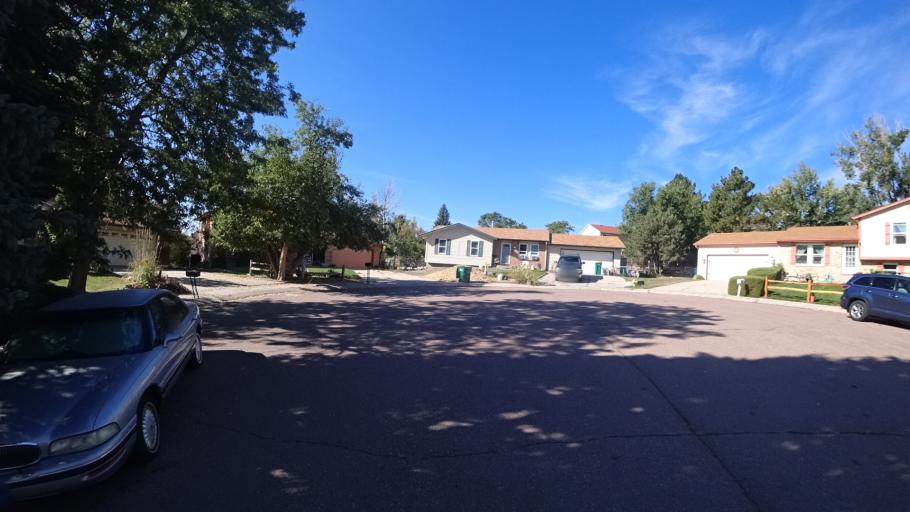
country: US
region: Colorado
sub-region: El Paso County
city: Colorado Springs
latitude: 38.9072
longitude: -104.7876
